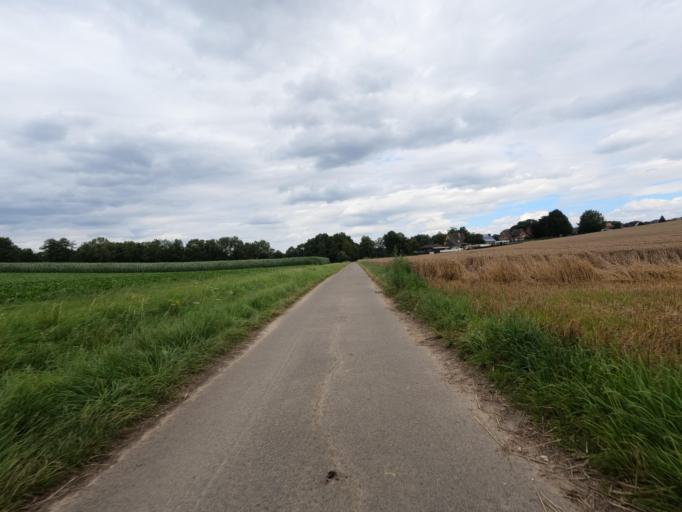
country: DE
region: North Rhine-Westphalia
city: Geilenkirchen
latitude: 50.9858
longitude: 6.1791
